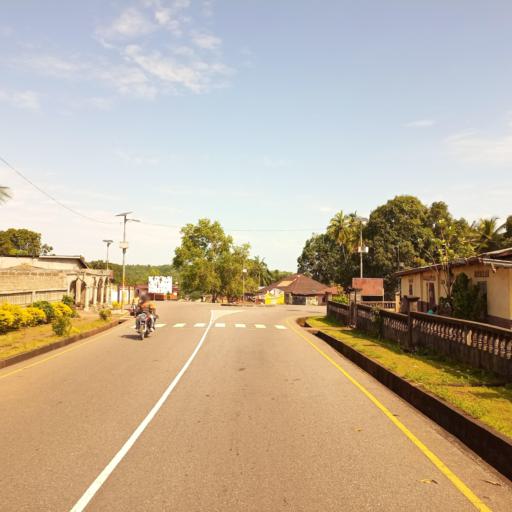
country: SL
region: Northern Province
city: Kambia
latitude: 9.1258
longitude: -12.9180
